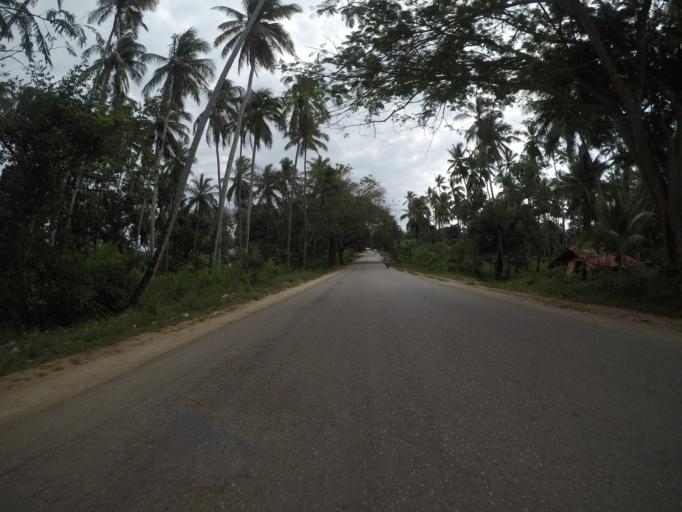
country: TZ
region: Zanzibar Central/South
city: Koani
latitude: -6.1953
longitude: 39.2924
